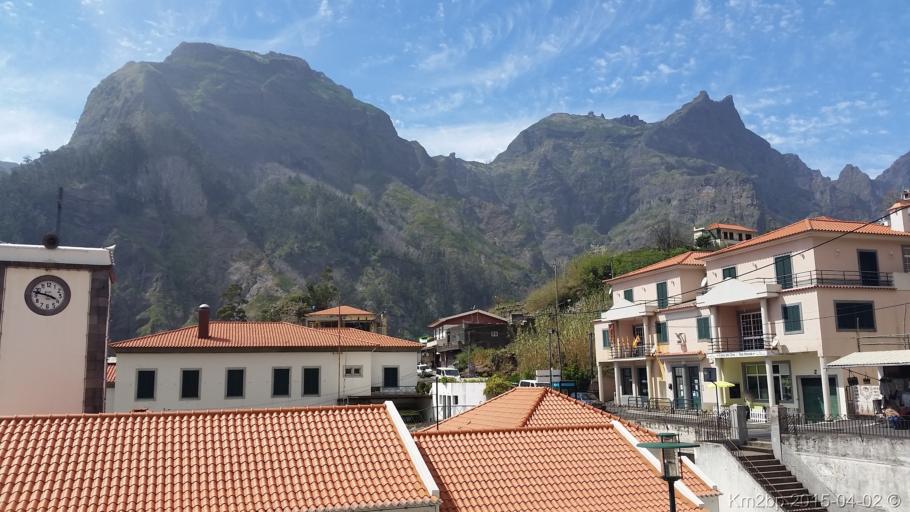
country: PT
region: Madeira
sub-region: Camara de Lobos
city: Curral das Freiras
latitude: 32.7203
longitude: -16.9655
